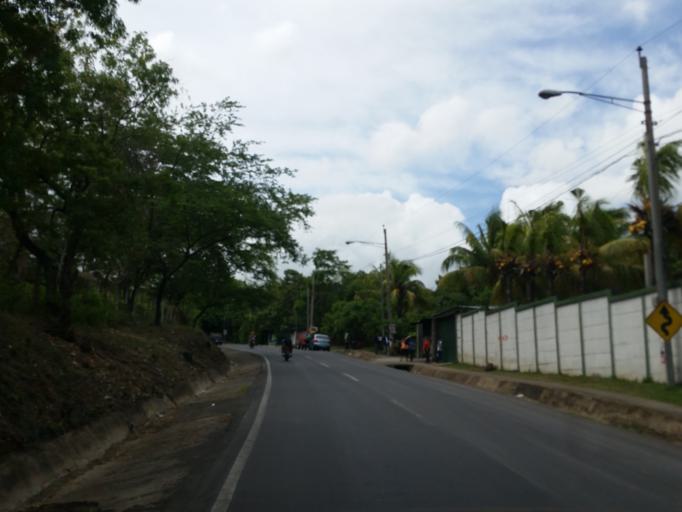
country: NI
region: Managua
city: Ciudad Sandino
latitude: 12.1063
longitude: -86.3253
